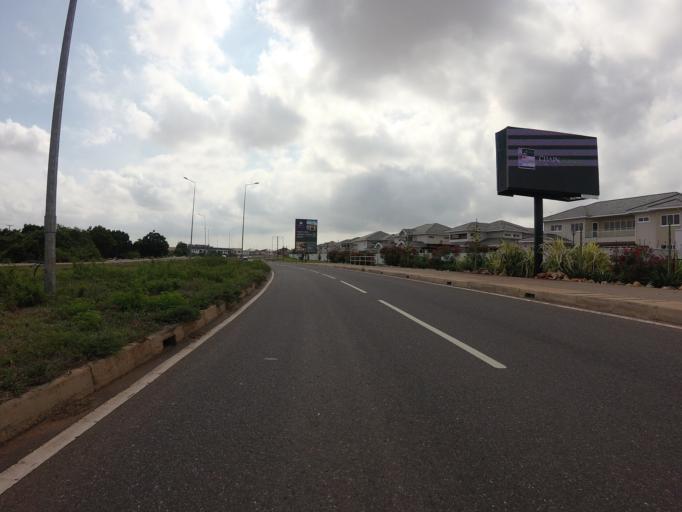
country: GH
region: Greater Accra
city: Teshi Old Town
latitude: 5.6101
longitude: -0.1449
